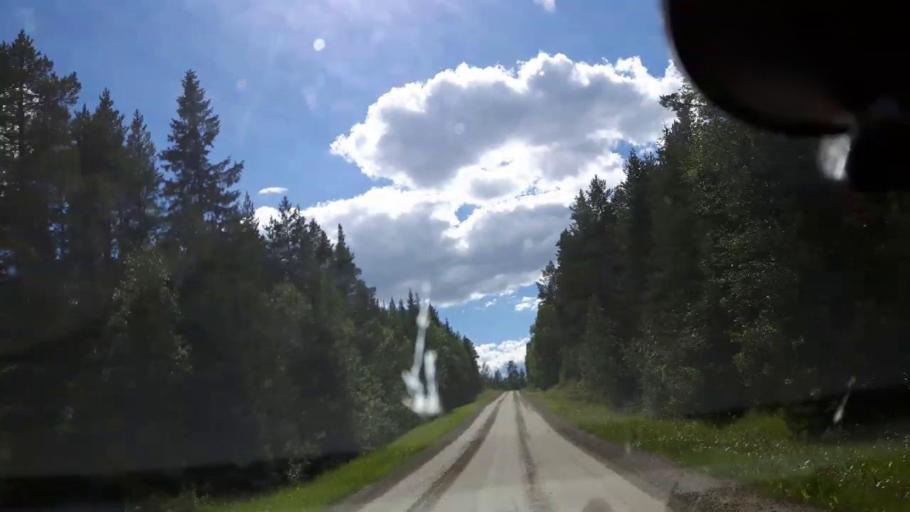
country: SE
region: Vaesternorrland
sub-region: Ange Kommun
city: Ange
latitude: 62.7202
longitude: 15.6340
